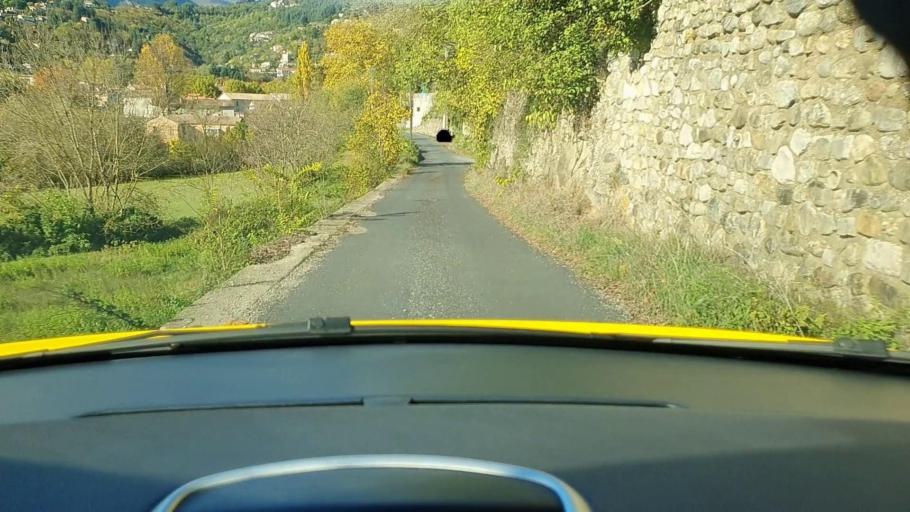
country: FR
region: Languedoc-Roussillon
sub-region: Departement du Gard
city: Le Vigan
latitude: 43.9866
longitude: 3.6088
